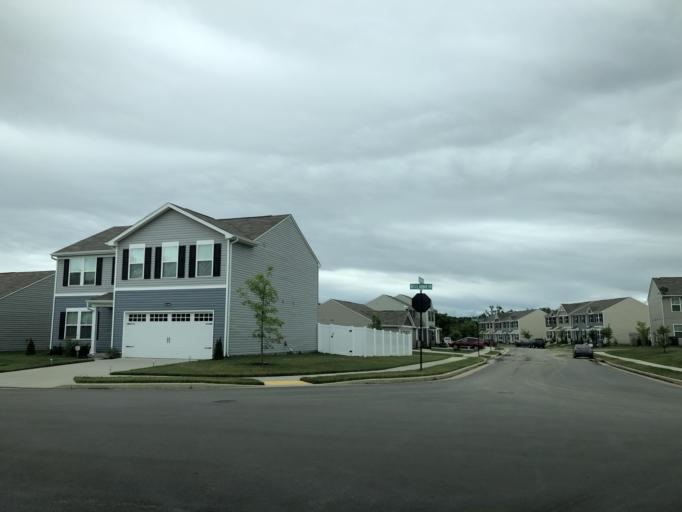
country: US
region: Tennessee
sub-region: Davidson County
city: Goodlettsville
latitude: 36.2575
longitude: -86.7721
